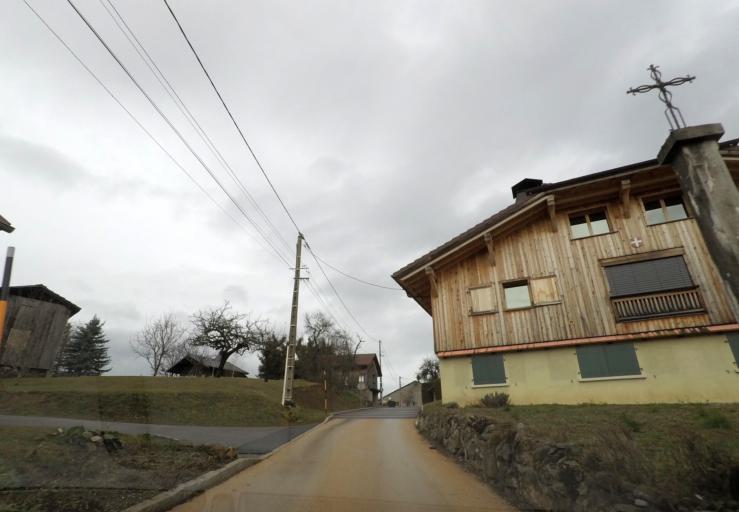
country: FR
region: Rhone-Alpes
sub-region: Departement de la Haute-Savoie
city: Chatillon-sur-Cluses
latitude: 46.0794
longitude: 6.6107
